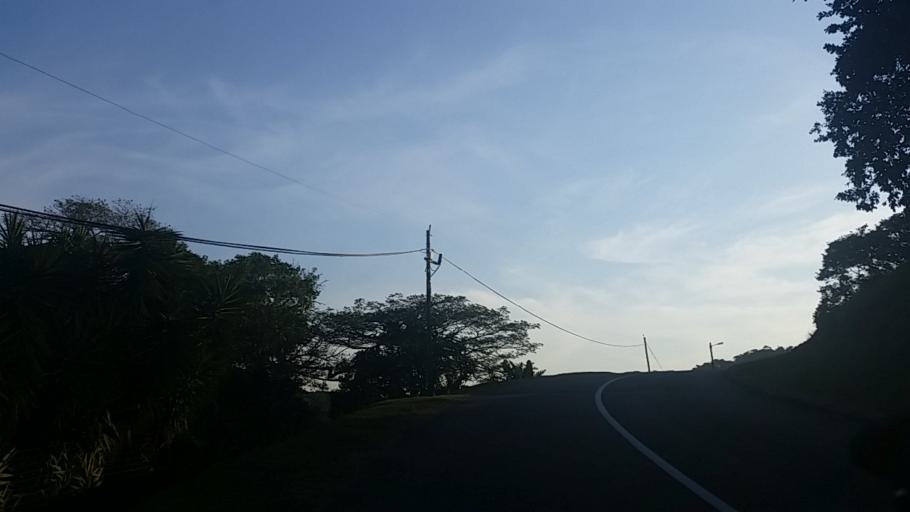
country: ZA
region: KwaZulu-Natal
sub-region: eThekwini Metropolitan Municipality
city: Berea
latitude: -29.8507
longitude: 30.9187
